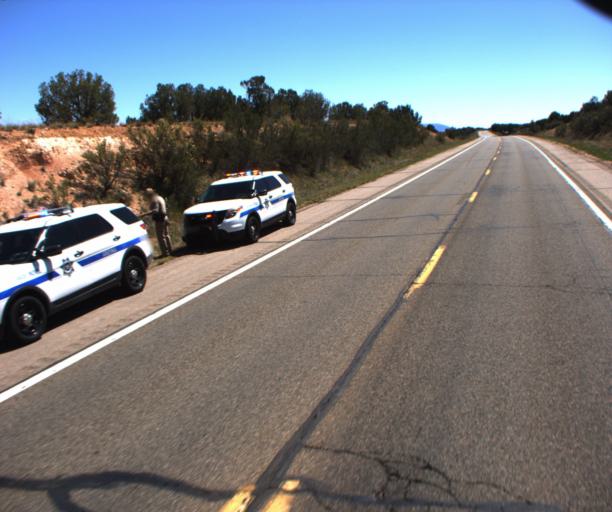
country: US
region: Arizona
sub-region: Yavapai County
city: Paulden
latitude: 34.9664
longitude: -112.4114
